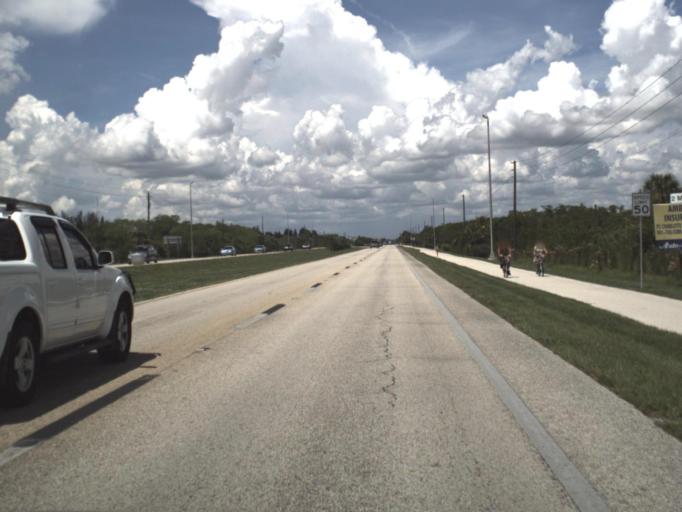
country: US
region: Florida
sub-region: Charlotte County
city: Charlotte Park
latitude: 26.8991
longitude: -82.0310
